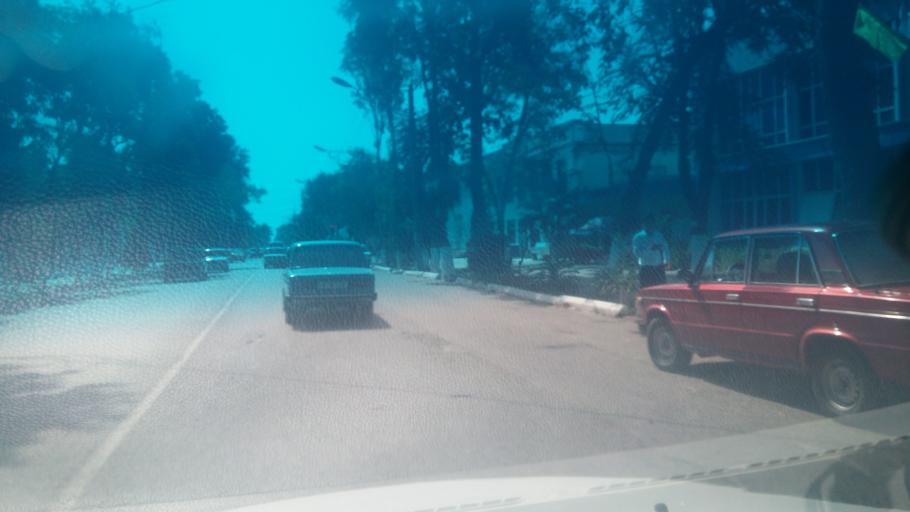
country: UZ
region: Sirdaryo
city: Sirdaryo
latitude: 40.8291
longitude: 68.6666
